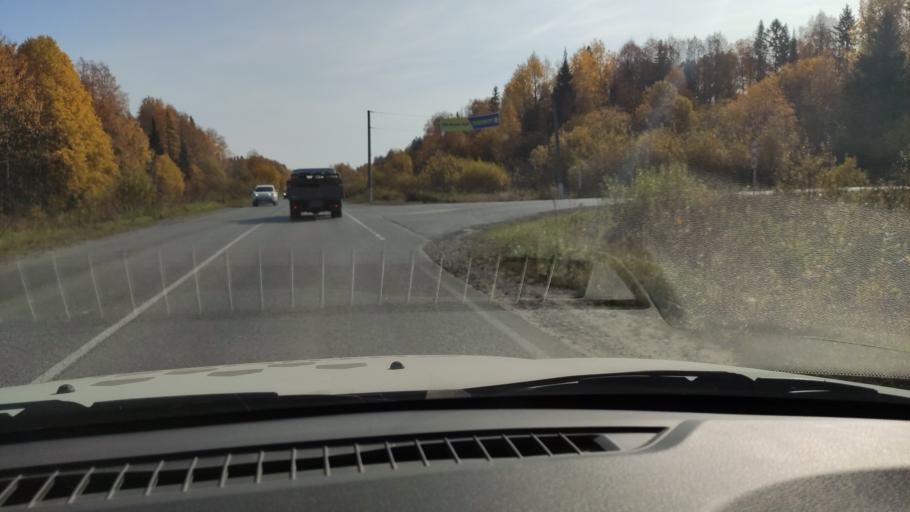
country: RU
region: Perm
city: Novyye Lyady
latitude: 58.0329
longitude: 56.6114
